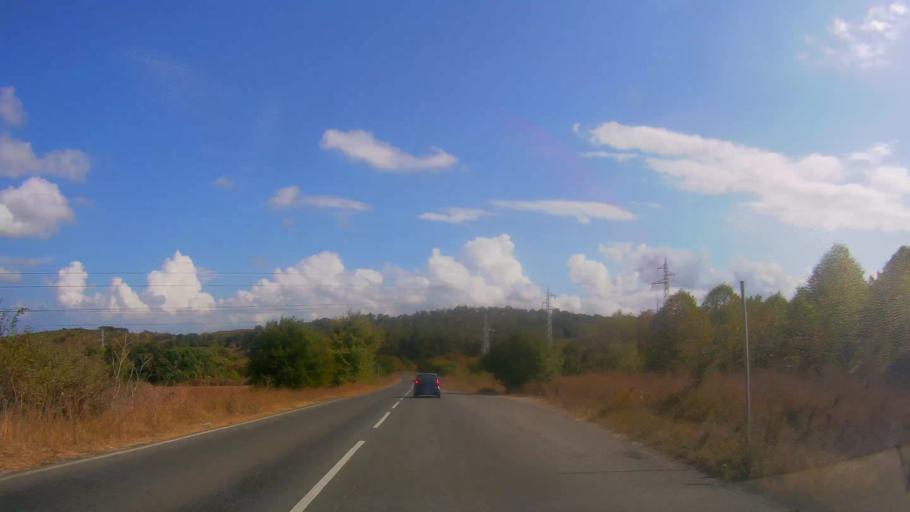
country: BG
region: Burgas
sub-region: Obshtina Burgas
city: Burgas
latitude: 42.4756
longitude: 27.3960
